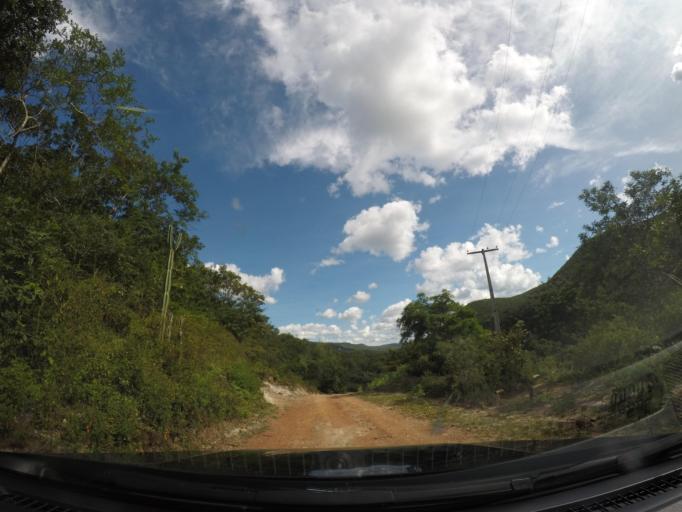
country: BR
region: Bahia
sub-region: Barra Da Estiva
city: Barra da Estiva
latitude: -13.1543
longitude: -41.5943
